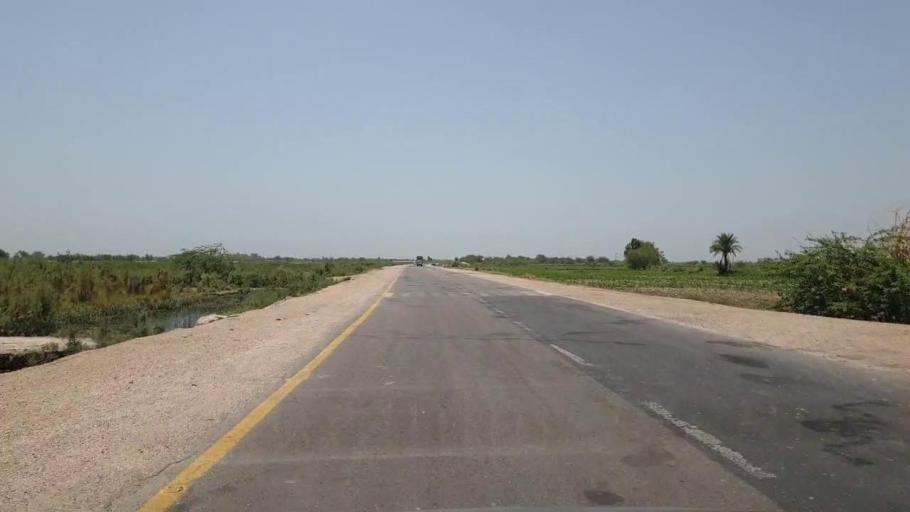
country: PK
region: Sindh
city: Sakrand
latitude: 26.1283
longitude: 68.3784
